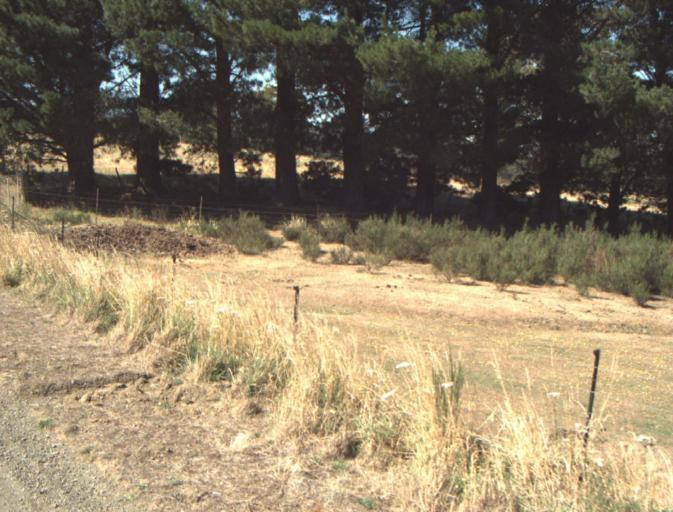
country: AU
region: Tasmania
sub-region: Launceston
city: Newstead
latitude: -41.3092
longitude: 147.3196
